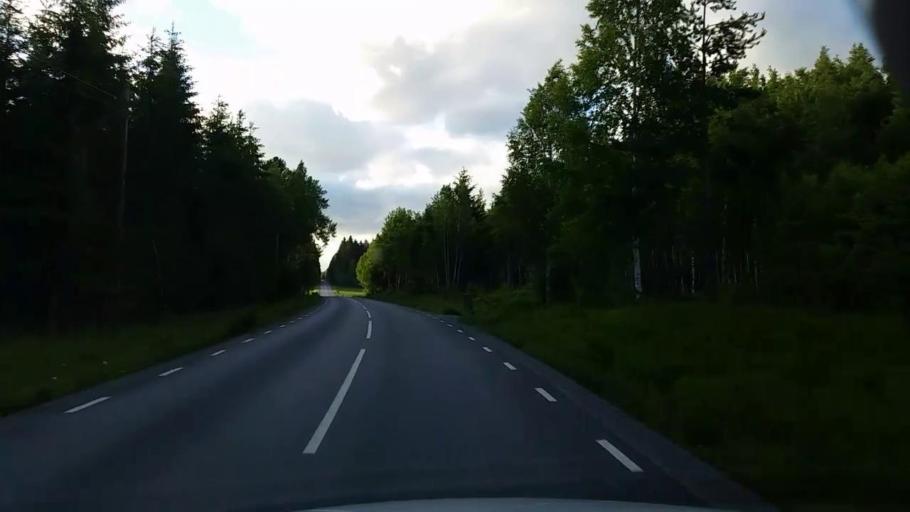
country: SE
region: Vaestmanland
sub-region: Kopings Kommun
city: Kolsva
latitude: 59.6787
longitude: 15.8418
